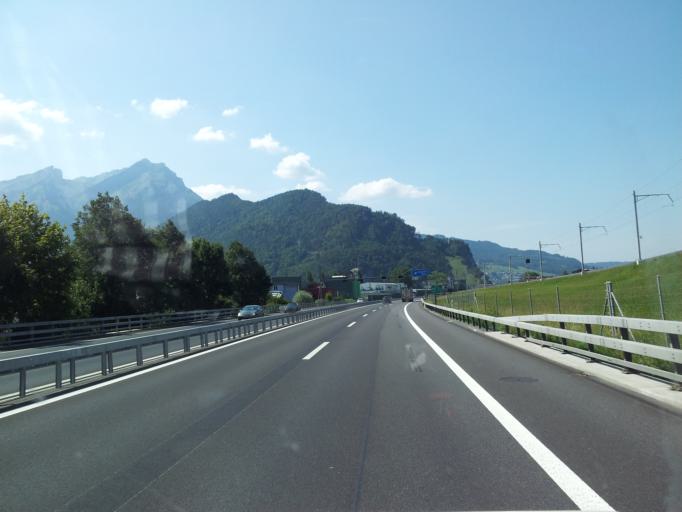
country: CH
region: Nidwalden
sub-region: Nidwalden
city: Stansstad
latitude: 46.9689
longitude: 8.3472
